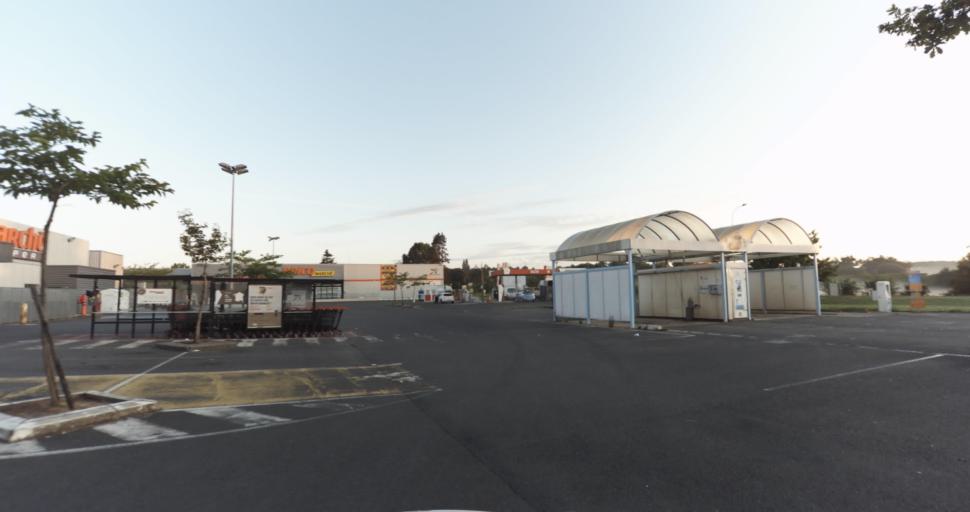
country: FR
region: Aquitaine
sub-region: Departement de la Gironde
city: Bazas
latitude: 44.4382
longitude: -0.2285
